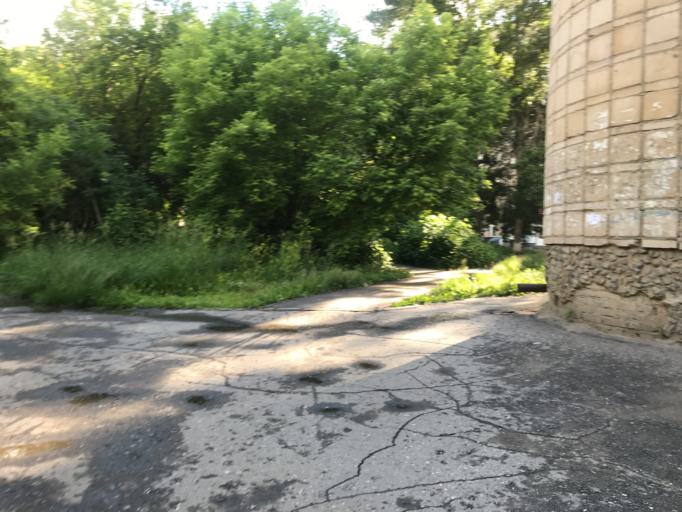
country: RU
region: Novosibirsk
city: Krasnoobsk
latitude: 54.9340
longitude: 82.9083
